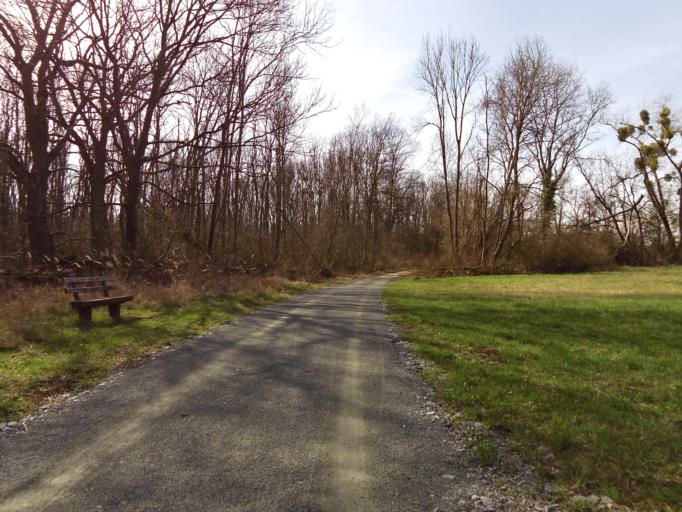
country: DE
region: Rheinland-Pfalz
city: Gimbsheim
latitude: 49.8059
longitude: 8.4150
